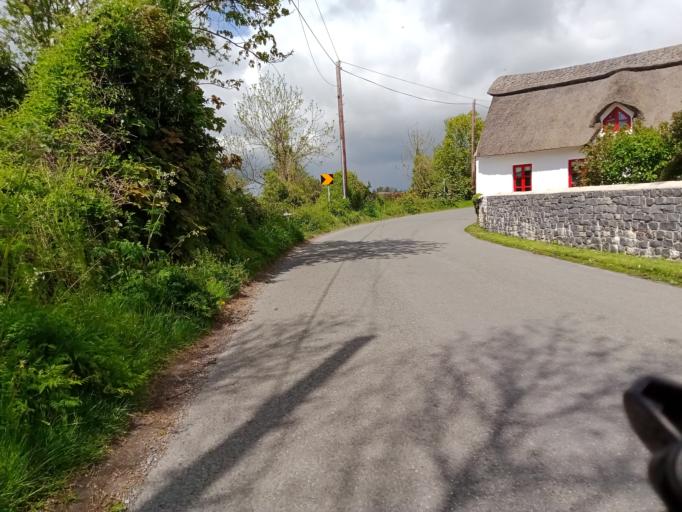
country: IE
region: Leinster
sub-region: Kilkenny
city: Kilkenny
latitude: 52.6699
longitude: -7.2601
